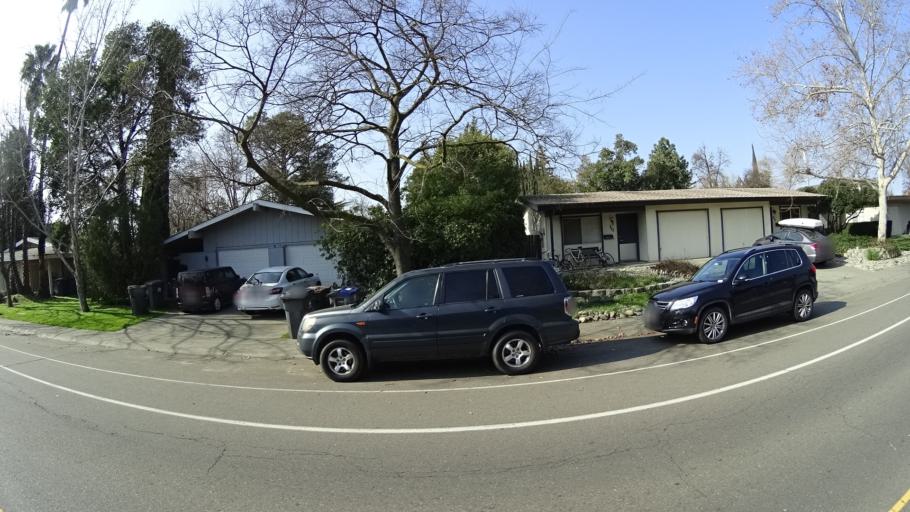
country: US
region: California
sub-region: Yolo County
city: Davis
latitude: 38.5501
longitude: -121.7704
